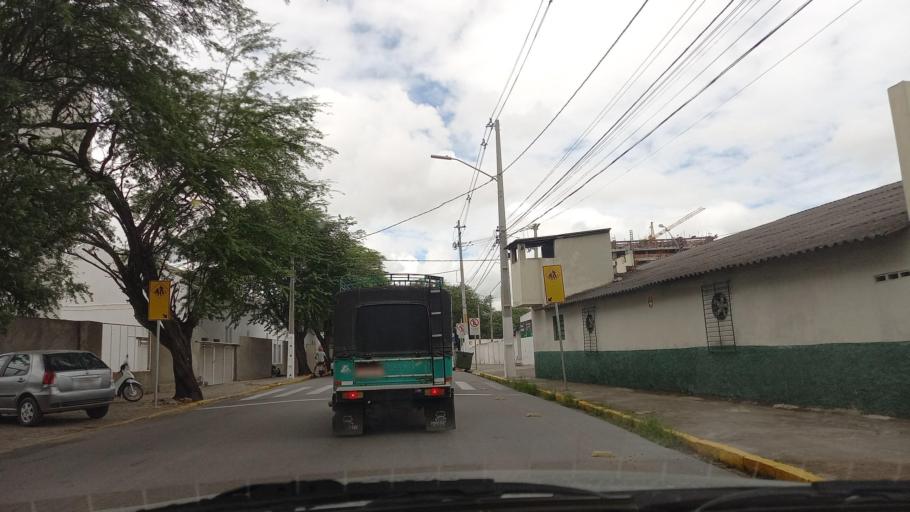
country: BR
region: Pernambuco
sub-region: Caruaru
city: Caruaru
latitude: -8.2818
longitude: -35.9679
